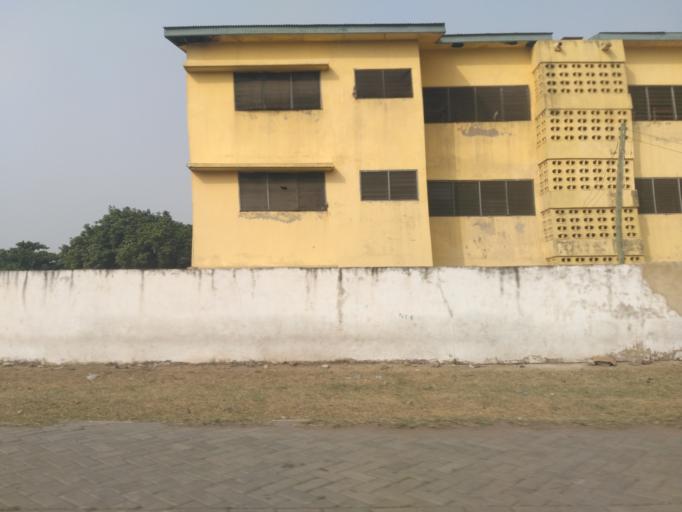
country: GH
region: Greater Accra
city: Accra
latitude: 5.5345
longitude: -0.2163
